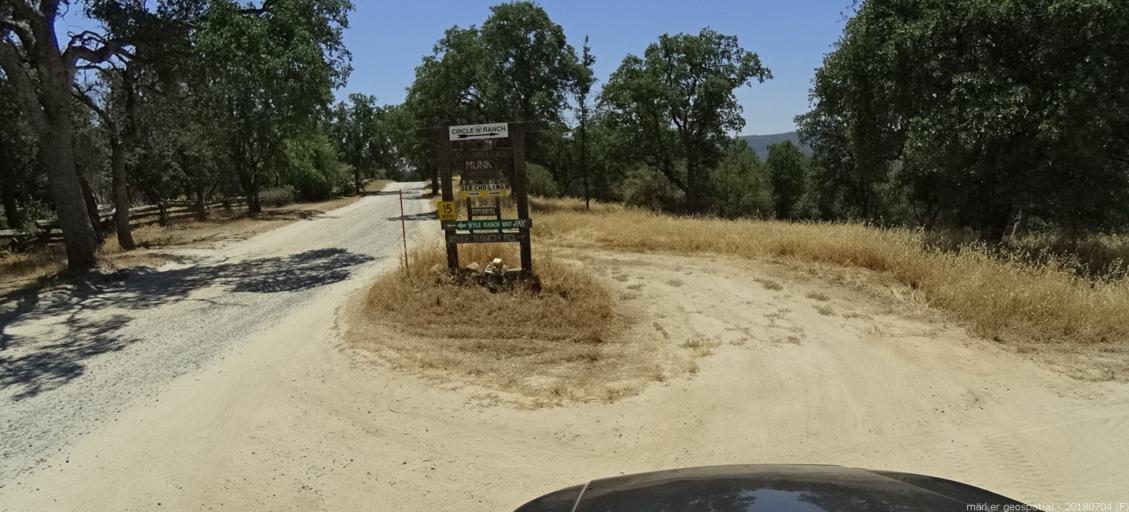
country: US
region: California
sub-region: Fresno County
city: Auberry
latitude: 37.2021
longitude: -119.5431
